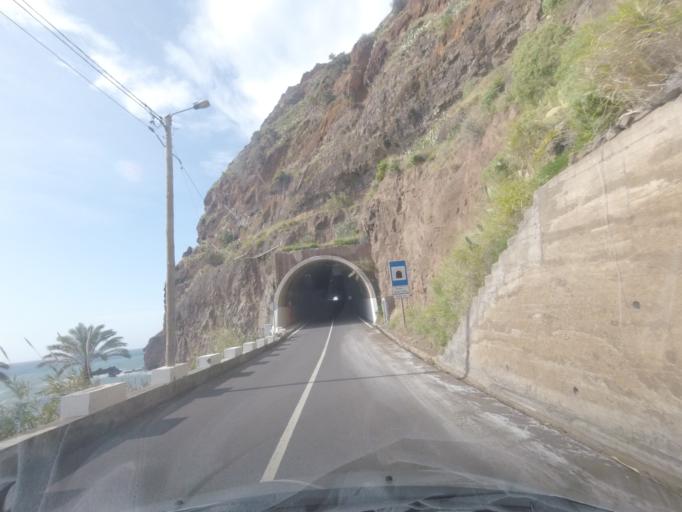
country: PT
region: Madeira
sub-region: Calheta
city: Arco da Calheta
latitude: 32.7035
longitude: -17.1376
